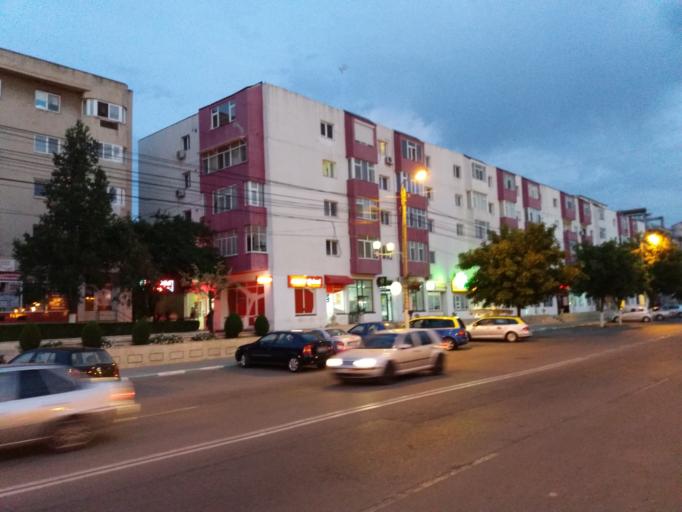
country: RO
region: Constanta
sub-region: Comuna Navodari
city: Navodari
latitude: 44.3226
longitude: 28.6098
